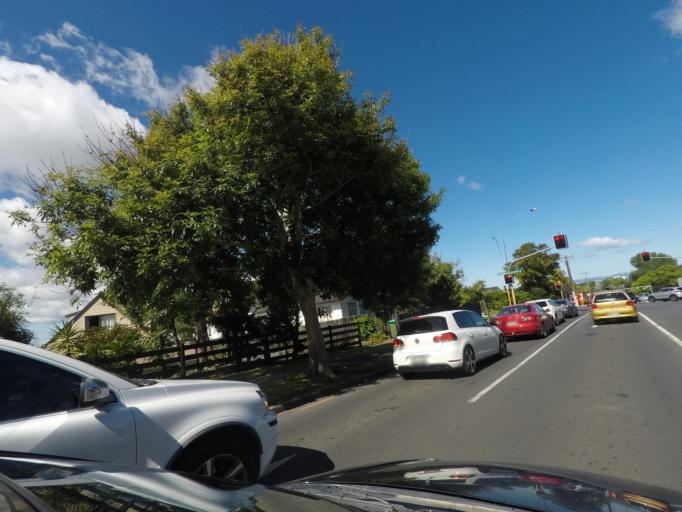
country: NZ
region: Auckland
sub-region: Auckland
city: Manukau City
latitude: -36.9900
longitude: 174.8968
